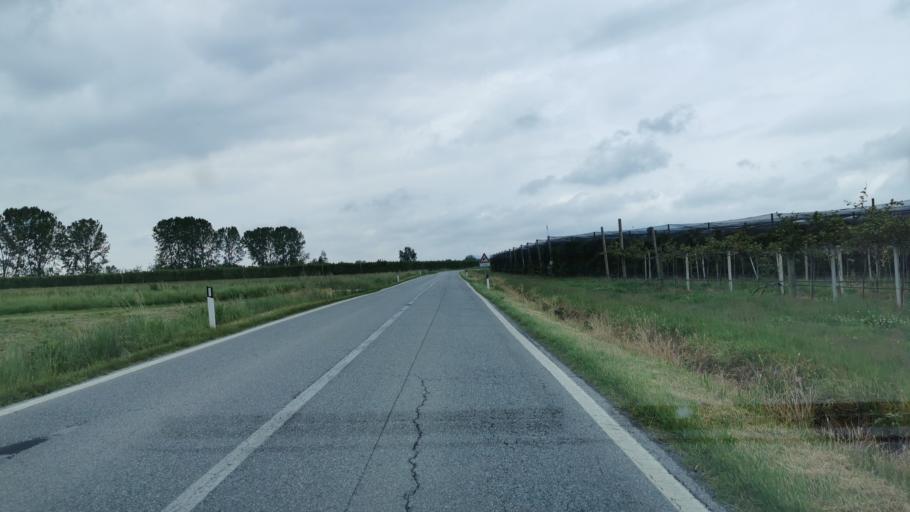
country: IT
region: Piedmont
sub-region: Provincia di Cuneo
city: Lagnasco
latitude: 44.5983
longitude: 7.5682
